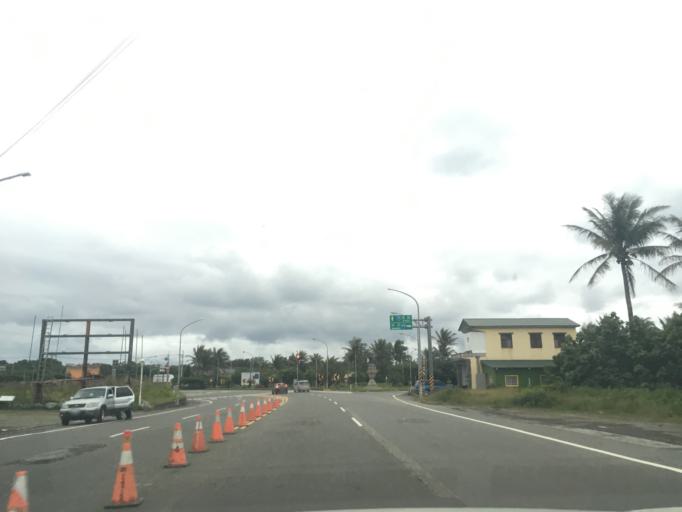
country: TW
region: Taiwan
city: Hengchun
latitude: 22.2947
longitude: 120.8868
